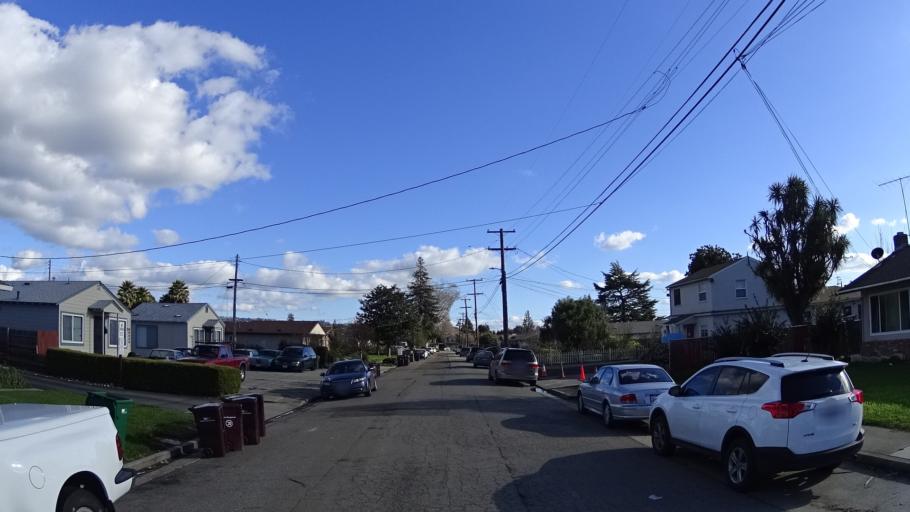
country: US
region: California
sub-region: Alameda County
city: Cherryland
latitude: 37.6776
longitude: -122.0951
